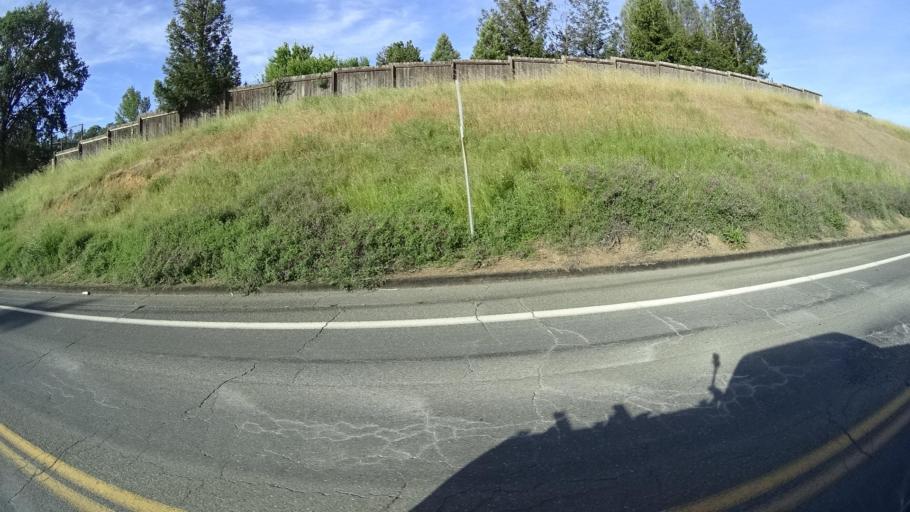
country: US
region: California
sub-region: Lake County
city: North Lakeport
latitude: 39.0813
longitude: -122.9221
